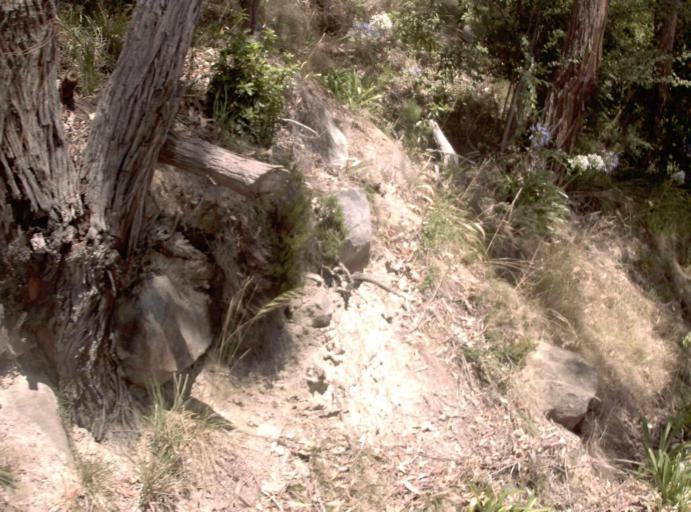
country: AU
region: Victoria
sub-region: Yarra Ranges
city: Kalorama
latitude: -37.8129
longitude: 145.3624
